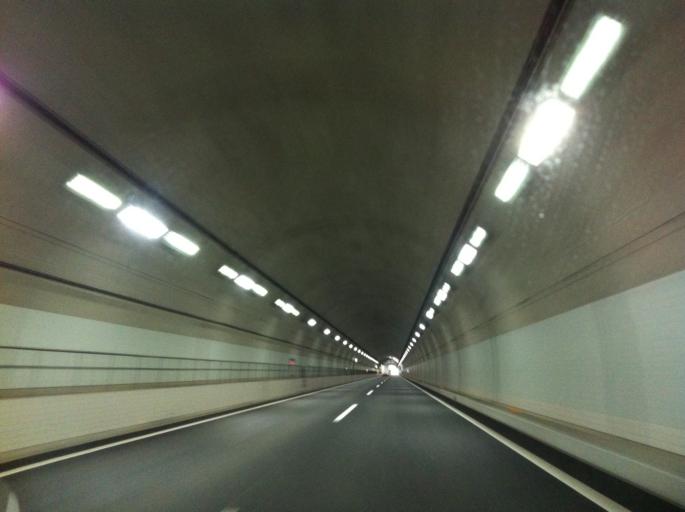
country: JP
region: Aichi
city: Shinshiro
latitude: 34.9015
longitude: 137.4476
